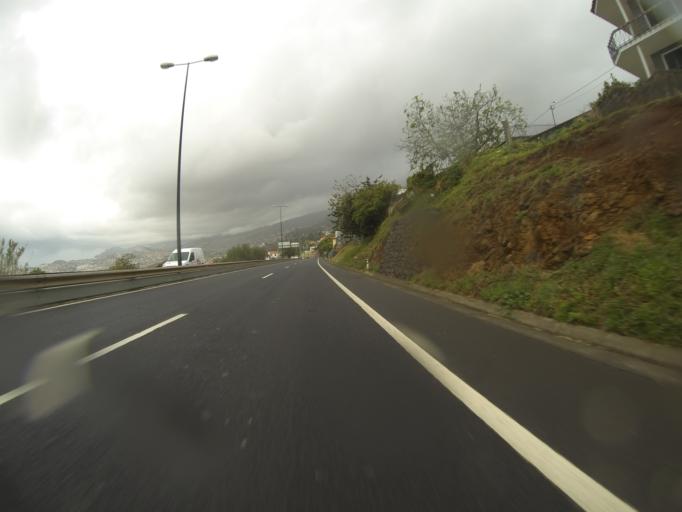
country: PT
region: Madeira
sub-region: Funchal
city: Nossa Senhora do Monte
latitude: 32.6591
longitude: -16.8892
